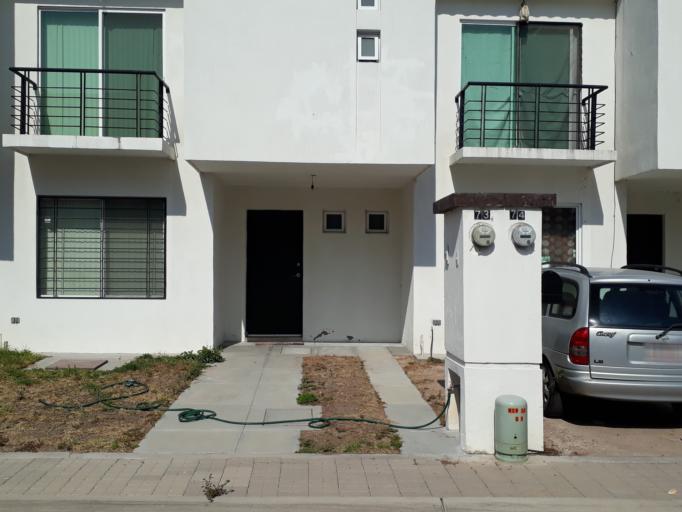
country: MX
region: Aguascalientes
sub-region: Aguascalientes
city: San Sebastian [Fraccionamiento]
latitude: 21.8032
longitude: -102.2951
